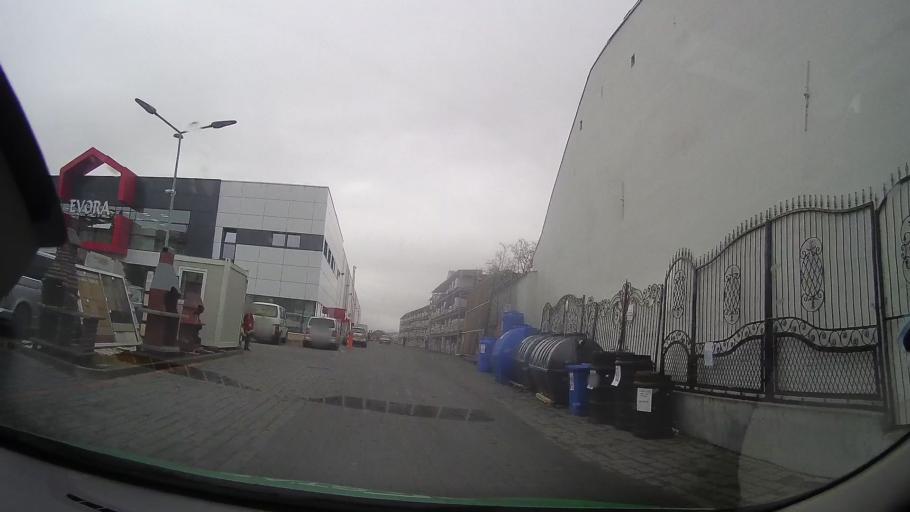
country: RO
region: Mures
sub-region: Municipiul Reghin
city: Reghin
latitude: 46.7855
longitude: 24.7049
